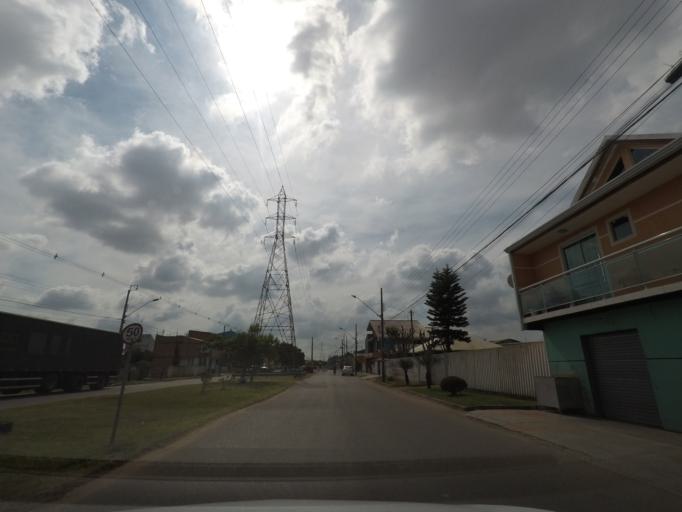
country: BR
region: Parana
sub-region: Pinhais
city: Pinhais
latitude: -25.4608
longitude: -49.1966
